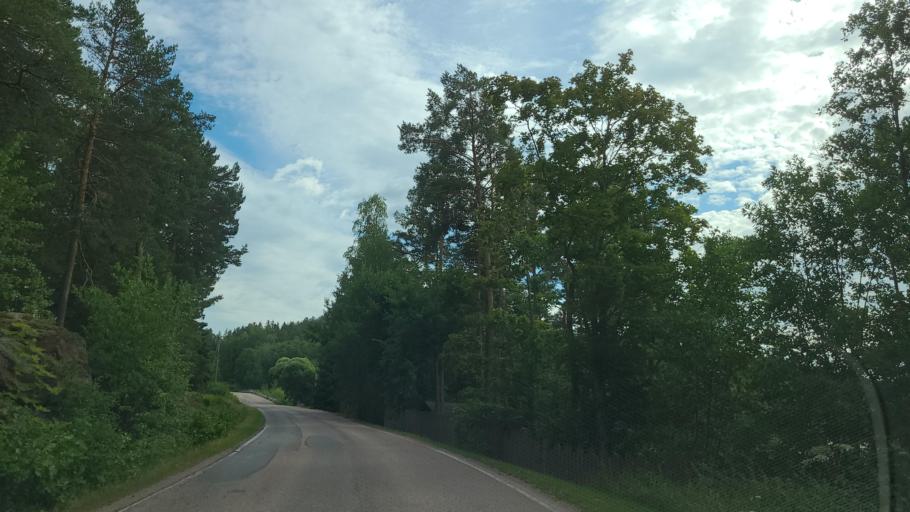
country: FI
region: Varsinais-Suomi
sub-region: Turku
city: Rymaettylae
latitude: 60.3426
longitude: 21.9780
